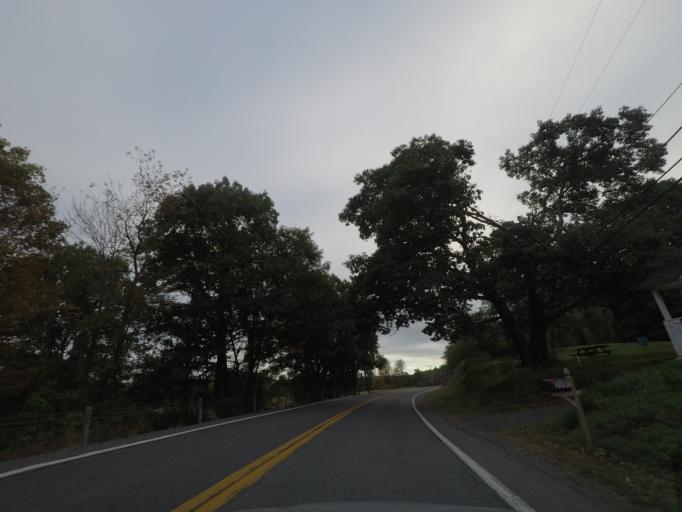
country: US
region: New York
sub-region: Rensselaer County
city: Nassau
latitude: 42.5727
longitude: -73.6243
